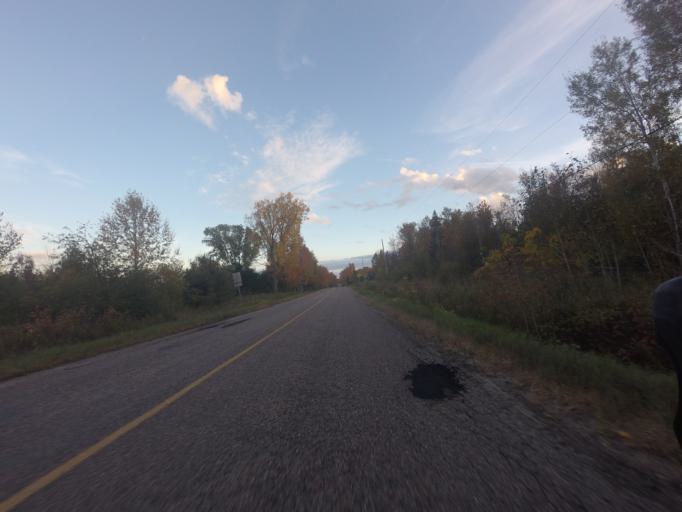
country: CA
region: Ontario
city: Renfrew
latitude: 45.4329
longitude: -76.9604
